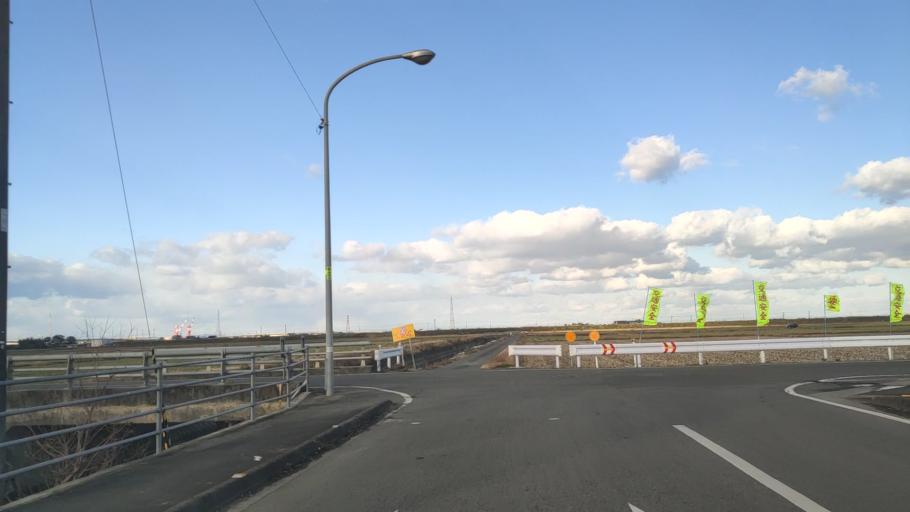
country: JP
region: Ehime
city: Saijo
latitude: 33.9032
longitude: 133.1360
